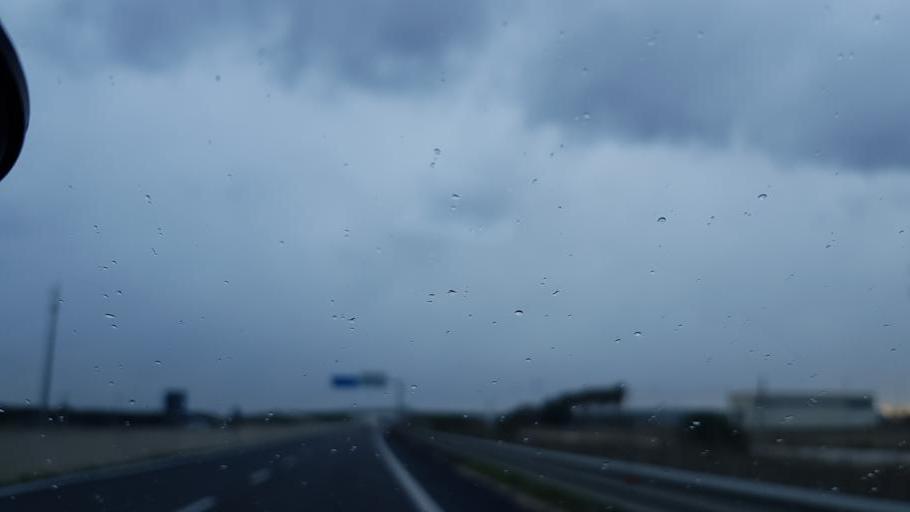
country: IT
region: Apulia
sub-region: Provincia di Brindisi
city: Mesagne
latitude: 40.5937
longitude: 17.8646
